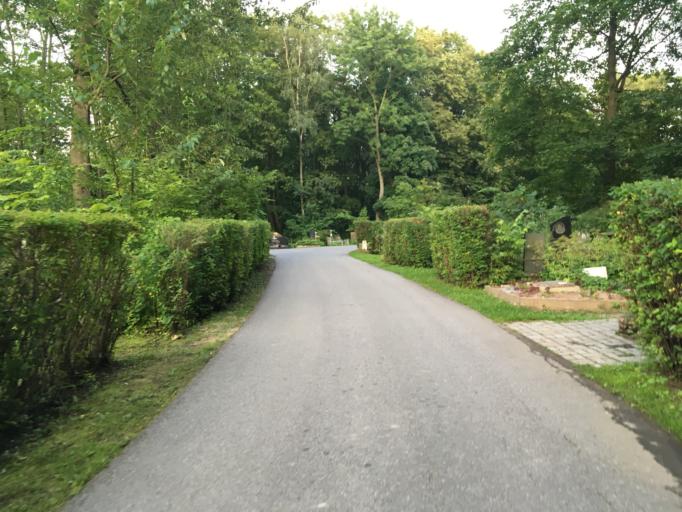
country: RU
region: St.-Petersburg
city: Centralniy
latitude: 59.9018
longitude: 30.3598
